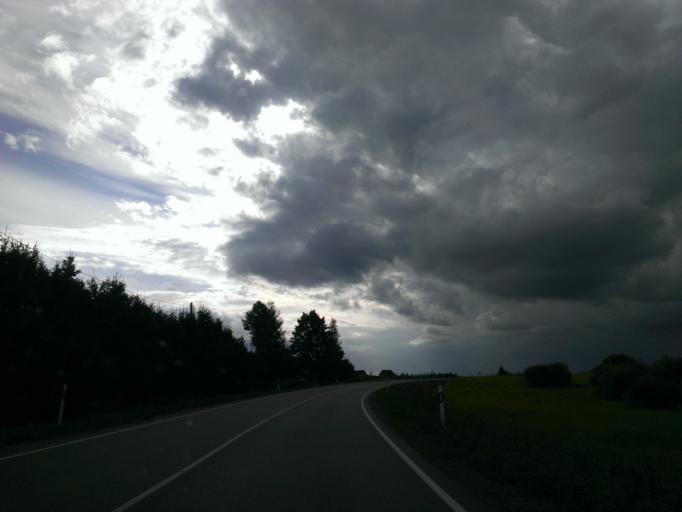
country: LV
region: Malpils
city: Malpils
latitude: 56.8927
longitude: 25.1617
